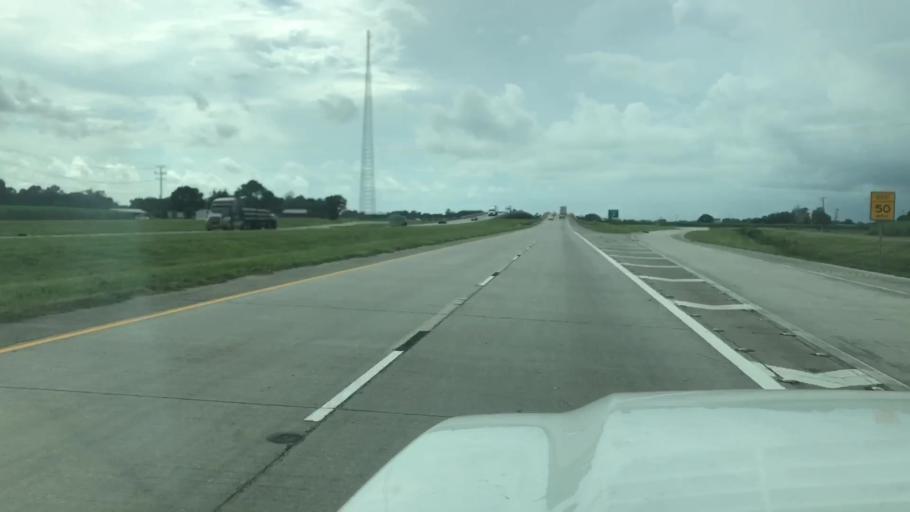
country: US
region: Louisiana
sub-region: Iberia Parish
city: Jeanerette
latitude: 29.9168
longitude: -91.7240
